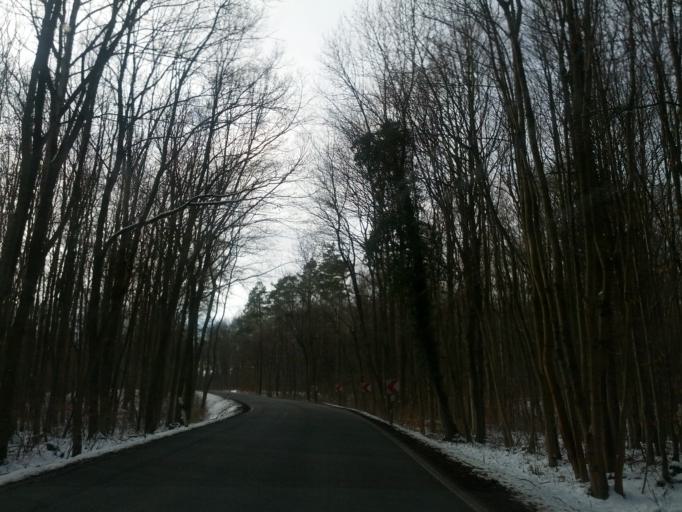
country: DE
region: Thuringia
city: Weberstedt
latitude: 51.0821
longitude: 10.5241
